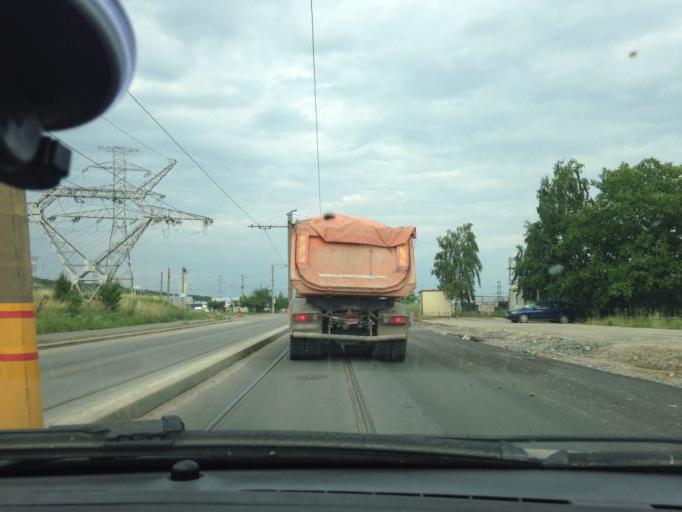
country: RO
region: Cluj
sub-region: Municipiul Cluj-Napoca
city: Cluj-Napoca
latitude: 46.7963
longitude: 23.6447
